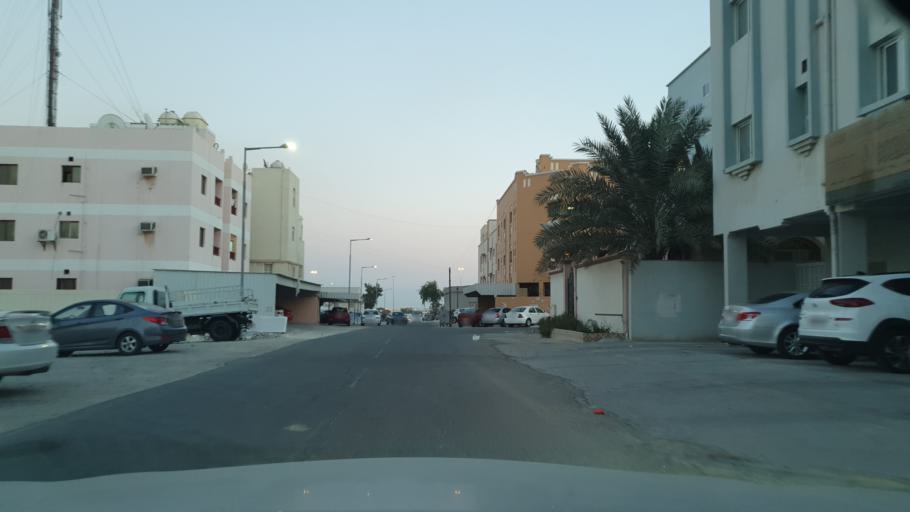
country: BH
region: Northern
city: Ar Rifa'
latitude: 26.1216
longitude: 50.5842
